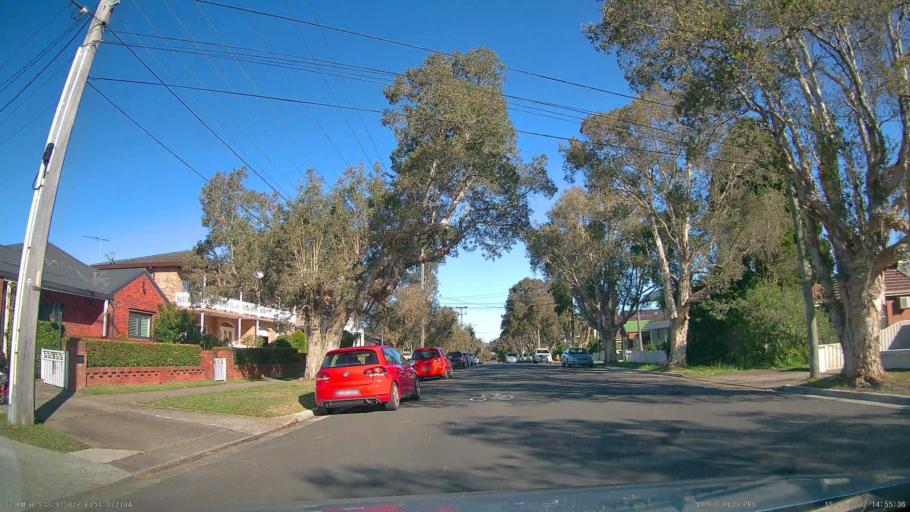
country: AU
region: New South Wales
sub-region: Hurstville
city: Oatley
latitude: -33.9759
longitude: 151.0722
